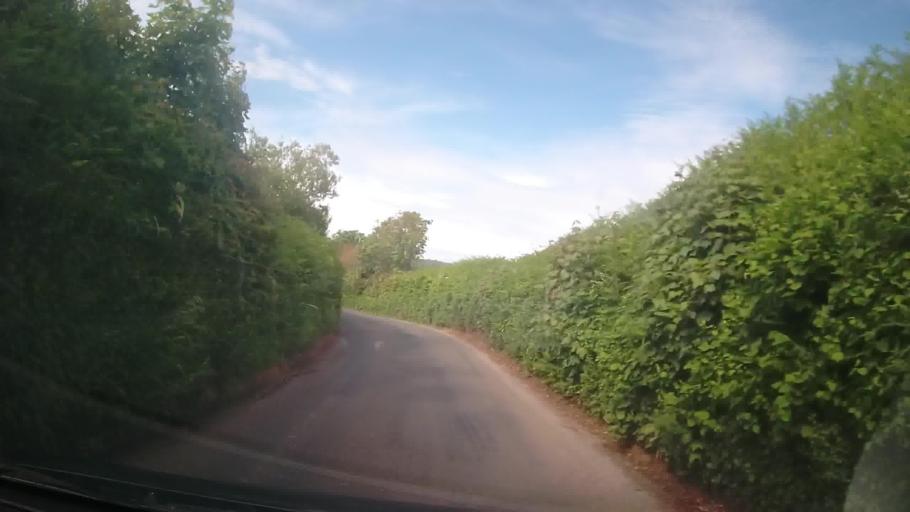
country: GB
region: England
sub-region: Devon
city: Salcombe
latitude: 50.2526
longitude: -3.6815
